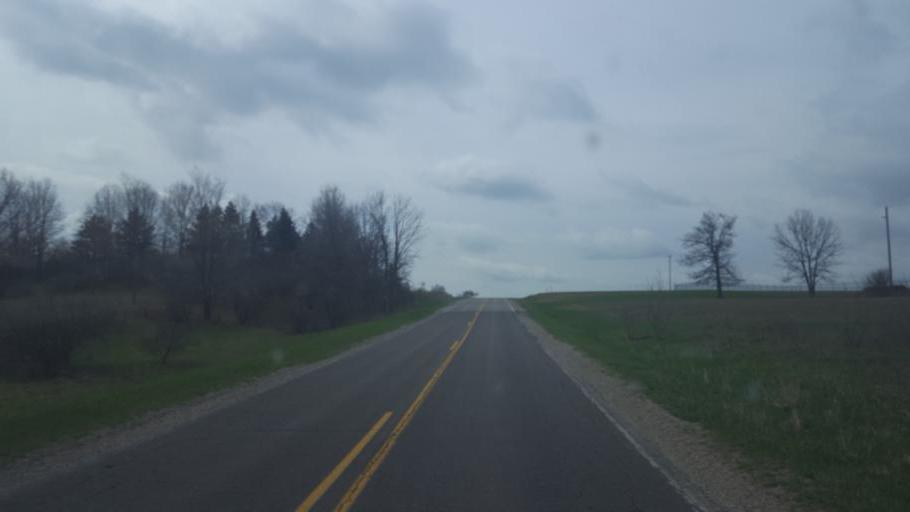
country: US
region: Michigan
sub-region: Montcalm County
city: Edmore
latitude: 43.4242
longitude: -85.0051
